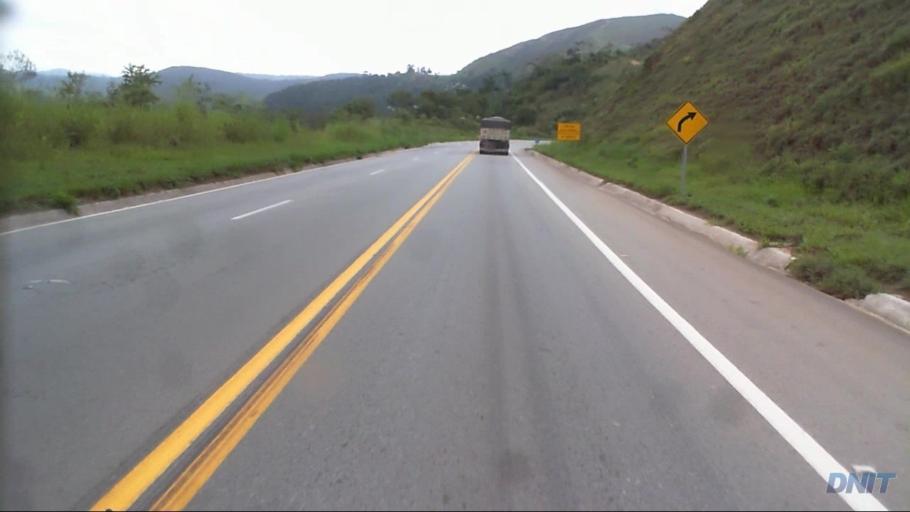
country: BR
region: Minas Gerais
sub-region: Nova Era
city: Nova Era
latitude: -19.6739
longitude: -42.9740
